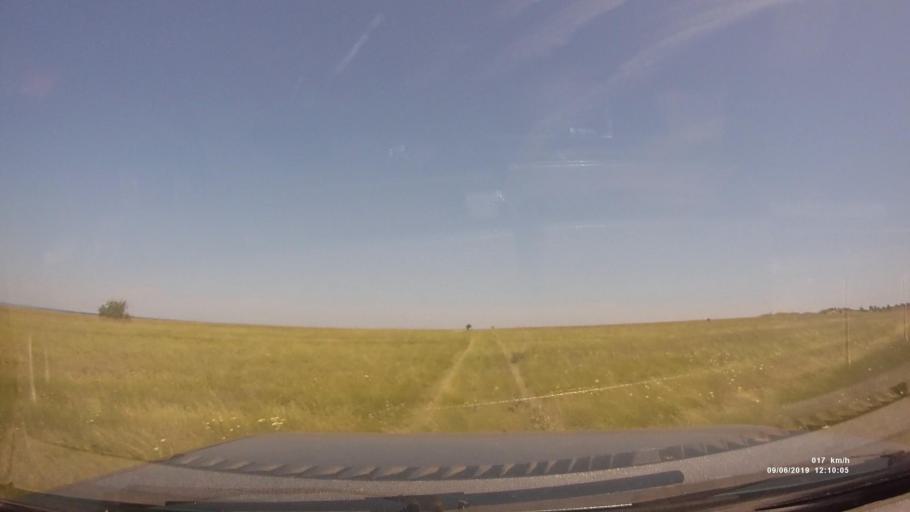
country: RU
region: Rostov
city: Staraya Stanitsa
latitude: 48.2494
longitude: 40.3386
